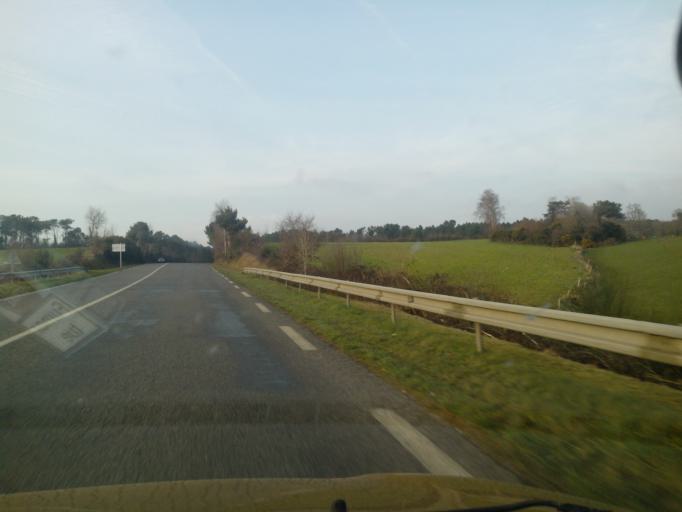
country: FR
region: Brittany
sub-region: Departement du Morbihan
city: Molac
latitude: 47.7046
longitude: -2.4442
